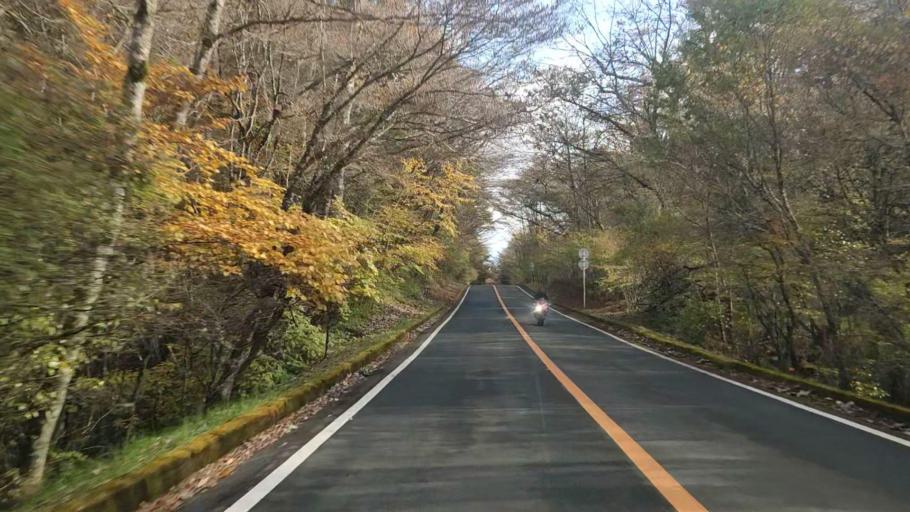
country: JP
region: Shizuoka
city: Fujinomiya
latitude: 35.3045
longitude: 138.6820
